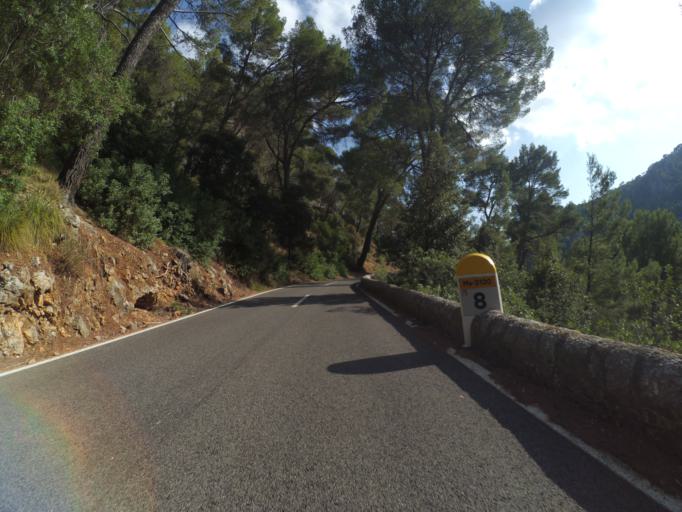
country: ES
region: Balearic Islands
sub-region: Illes Balears
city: Selva
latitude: 39.7782
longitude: 2.8984
